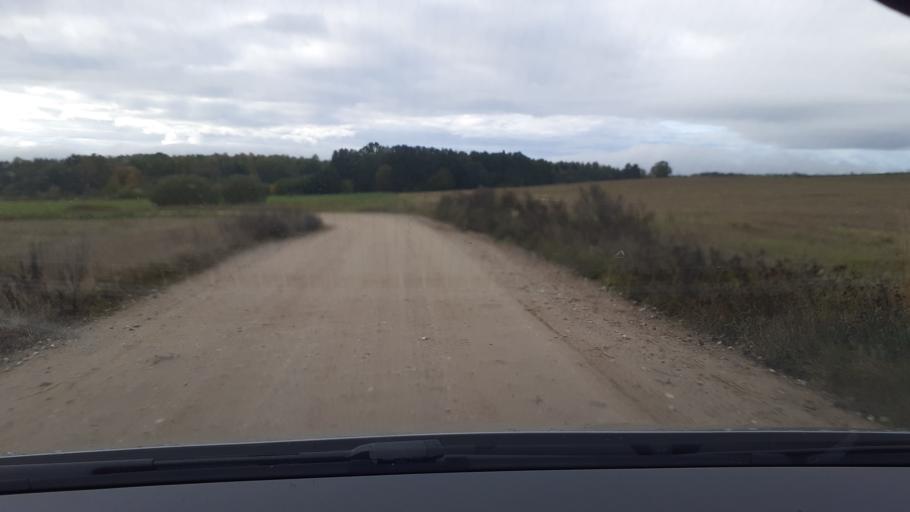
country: LV
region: Kuldigas Rajons
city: Kuldiga
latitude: 57.0143
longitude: 21.9153
